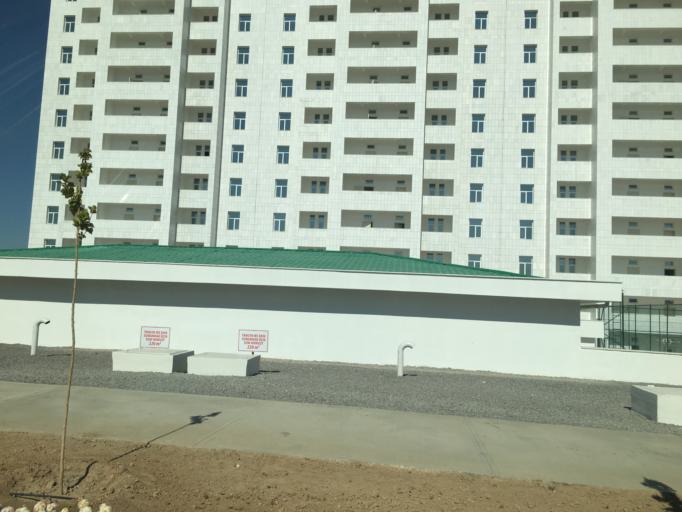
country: TM
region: Ahal
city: Ashgabat
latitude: 37.9384
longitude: 58.3580
